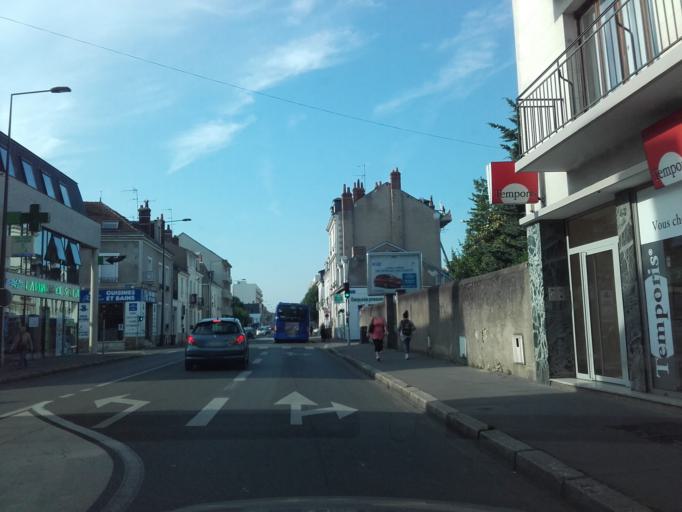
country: FR
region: Centre
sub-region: Departement d'Indre-et-Loire
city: La Riche
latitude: 47.3865
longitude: 0.6766
